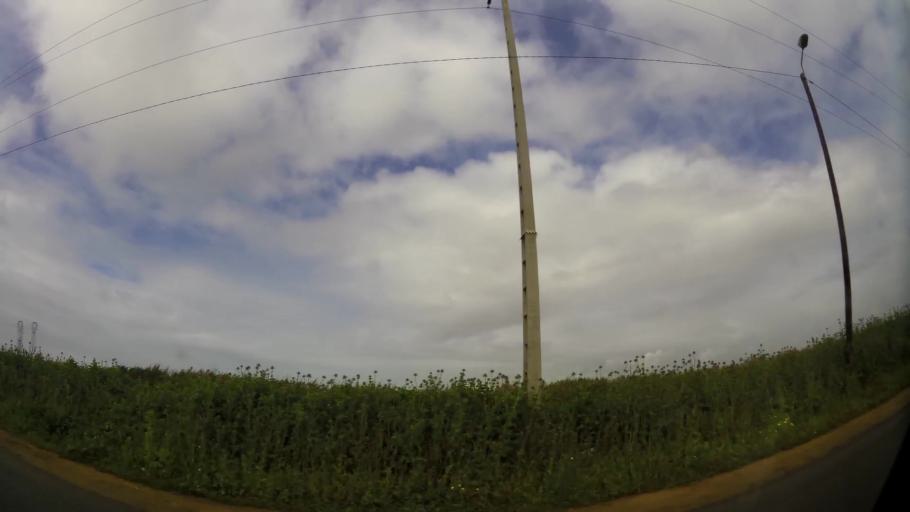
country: MA
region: Grand Casablanca
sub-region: Mohammedia
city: Mohammedia
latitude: 33.6497
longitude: -7.4569
